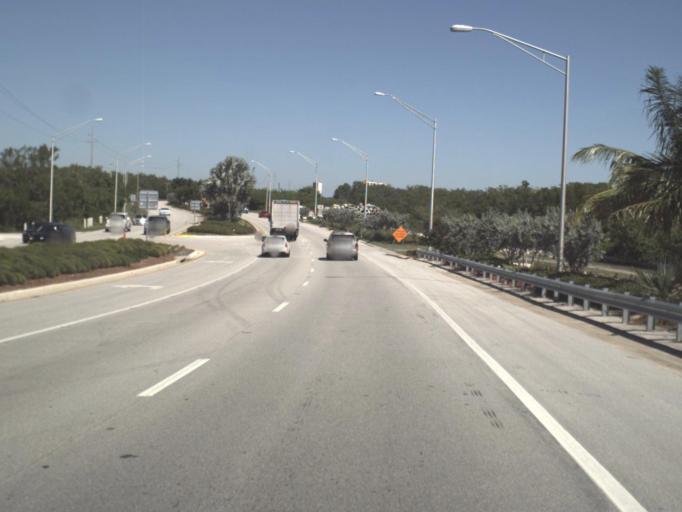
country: US
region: Florida
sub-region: Collier County
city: Marco
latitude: 25.9662
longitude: -81.7084
